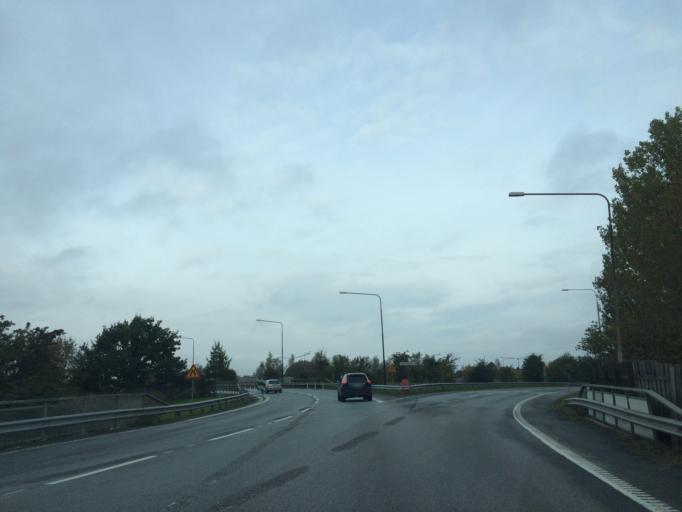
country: SE
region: Skane
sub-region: Malmo
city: Malmoe
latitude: 55.5652
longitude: 13.0035
